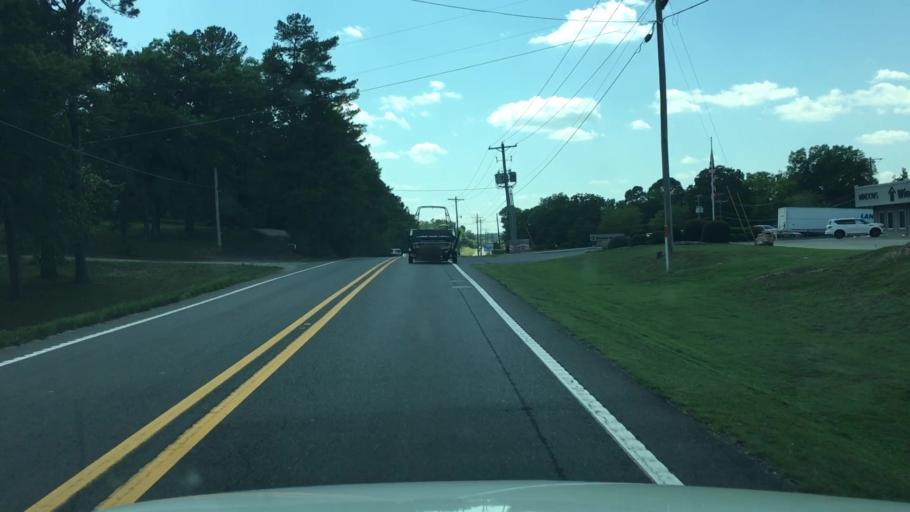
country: US
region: Arkansas
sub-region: Garland County
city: Piney
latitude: 34.5105
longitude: -93.2065
